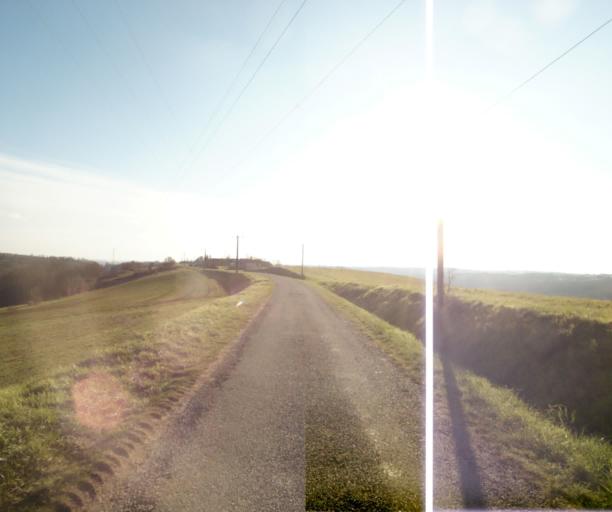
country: FR
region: Midi-Pyrenees
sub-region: Departement du Tarn-et-Garonne
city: Moissac
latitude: 44.1424
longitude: 1.1117
